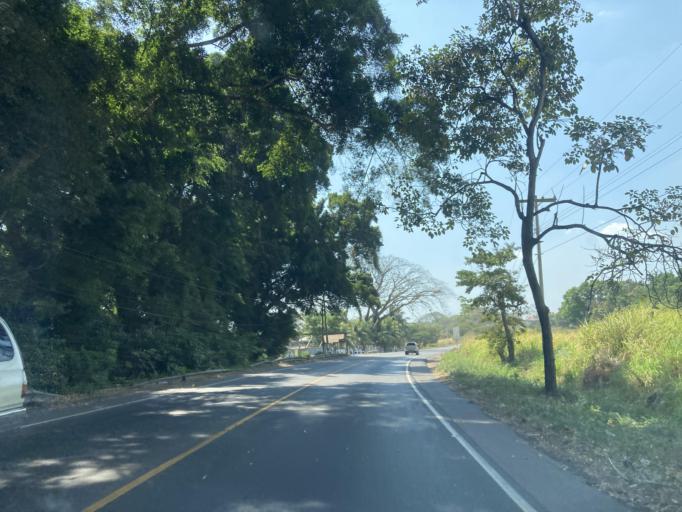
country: GT
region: Escuintla
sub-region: Municipio de Escuintla
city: Escuintla
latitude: 14.2438
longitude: -90.7405
